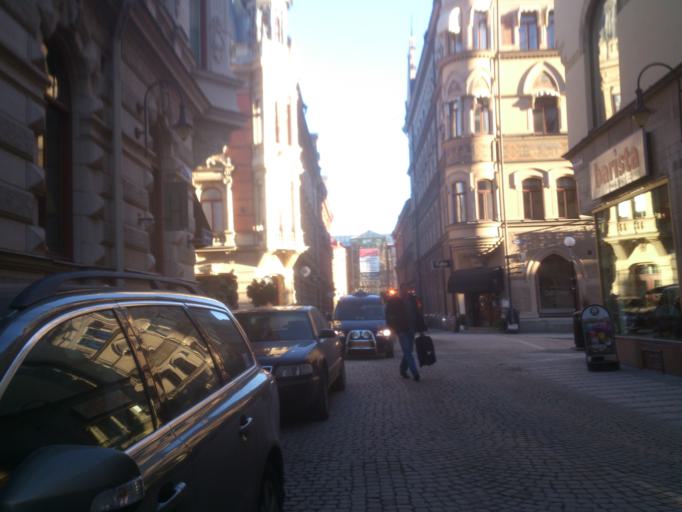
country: SE
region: Vaesternorrland
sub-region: Sundsvalls Kommun
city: Sundsvall
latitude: 62.3904
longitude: 17.3115
